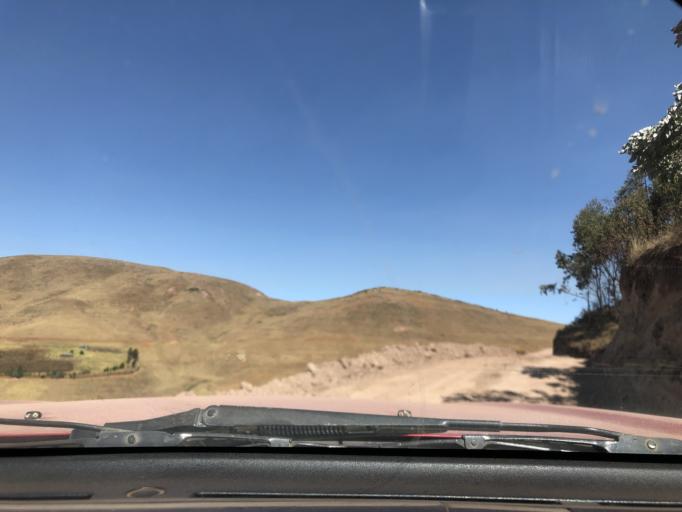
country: PE
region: Ayacucho
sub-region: Provincia de La Mar
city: Chilcas
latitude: -13.1823
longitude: -73.8402
